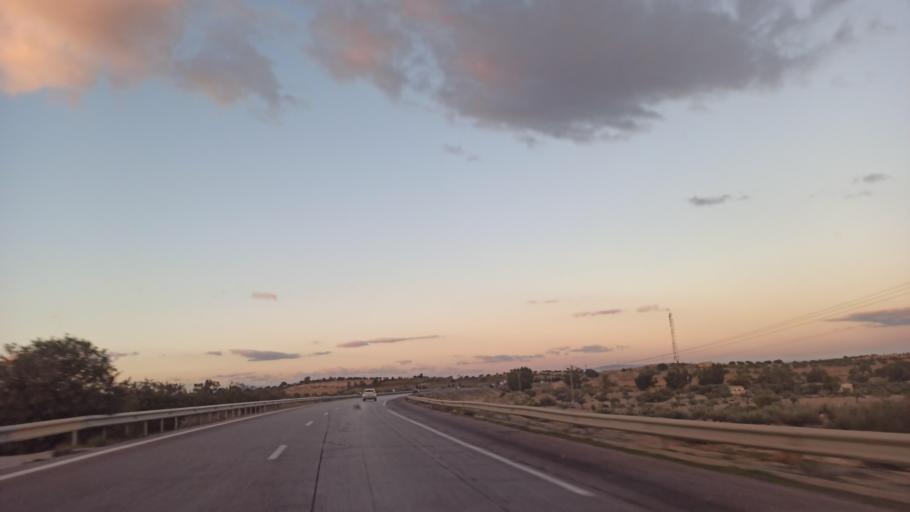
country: TN
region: Susah
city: Harqalah
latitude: 36.2333
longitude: 10.4133
